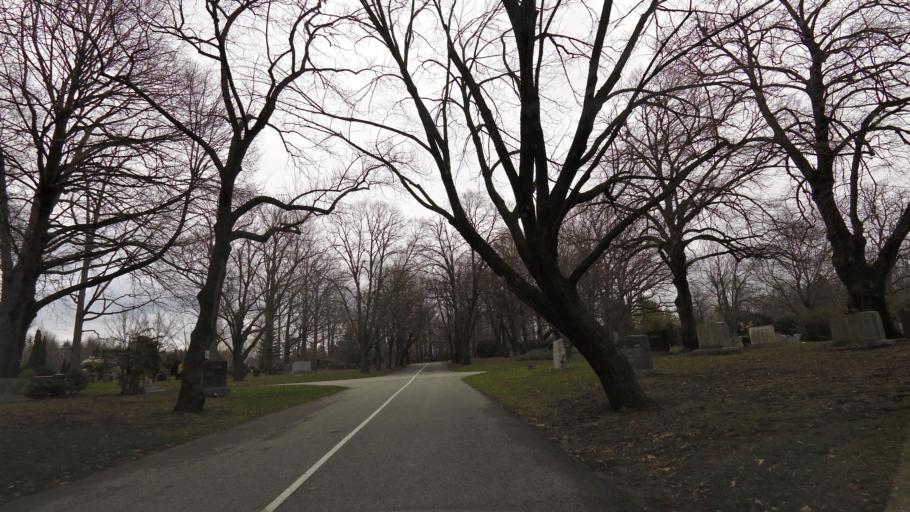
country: CA
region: Ontario
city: Toronto
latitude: 43.6977
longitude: -79.3804
